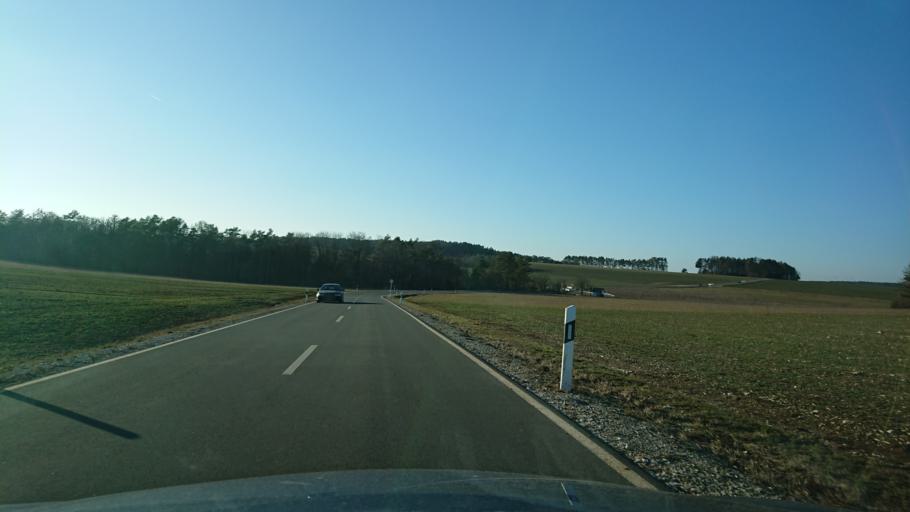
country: DE
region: Bavaria
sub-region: Upper Franconia
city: Ebermannstadt
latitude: 49.7949
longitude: 11.1533
